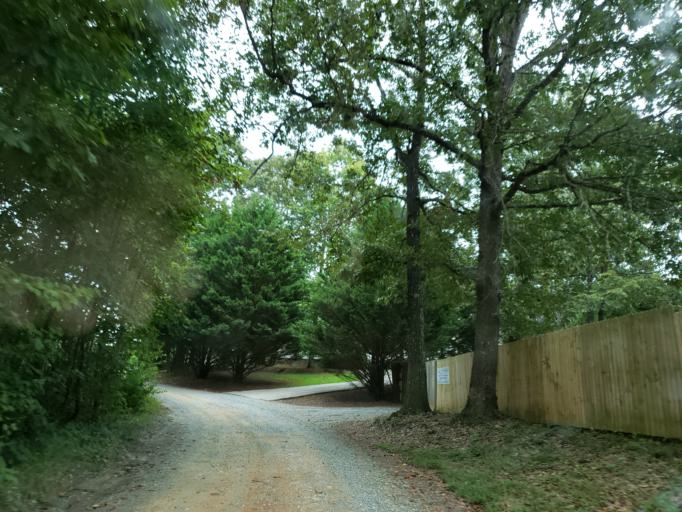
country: US
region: Georgia
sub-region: Gilmer County
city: Ellijay
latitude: 34.6051
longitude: -84.5684
